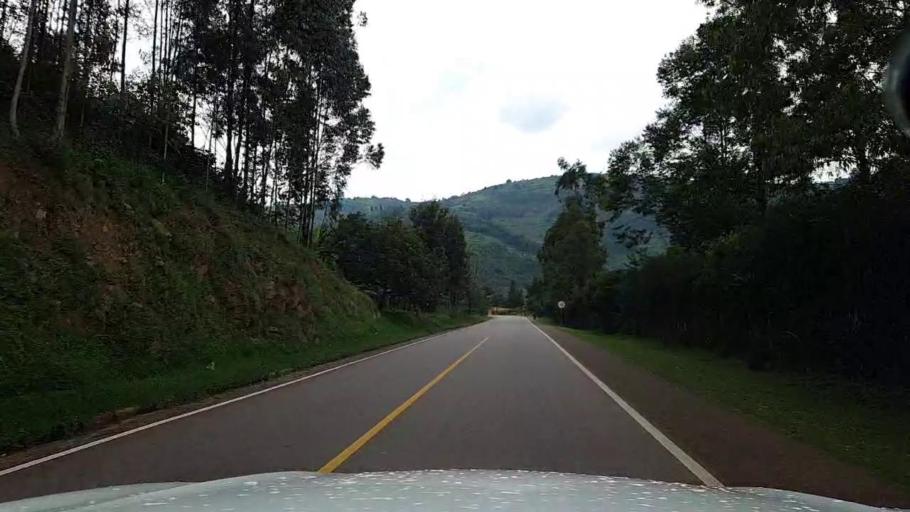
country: RW
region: Northern Province
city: Byumba
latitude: -1.7154
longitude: 30.1228
